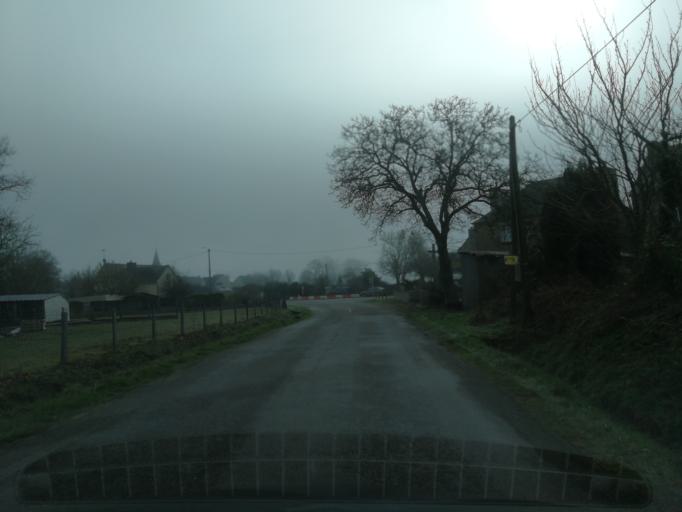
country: FR
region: Brittany
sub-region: Departement du Morbihan
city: La Vraie-Croix
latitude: 47.7435
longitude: -2.5045
